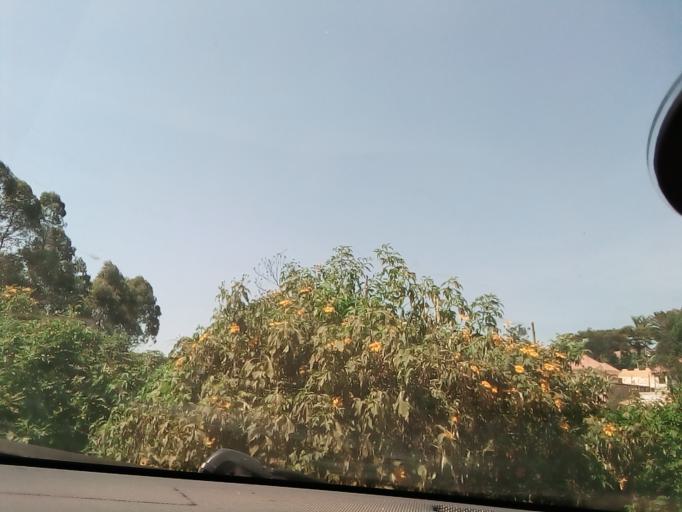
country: UG
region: Central Region
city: Masaka
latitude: -0.3483
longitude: 31.7447
